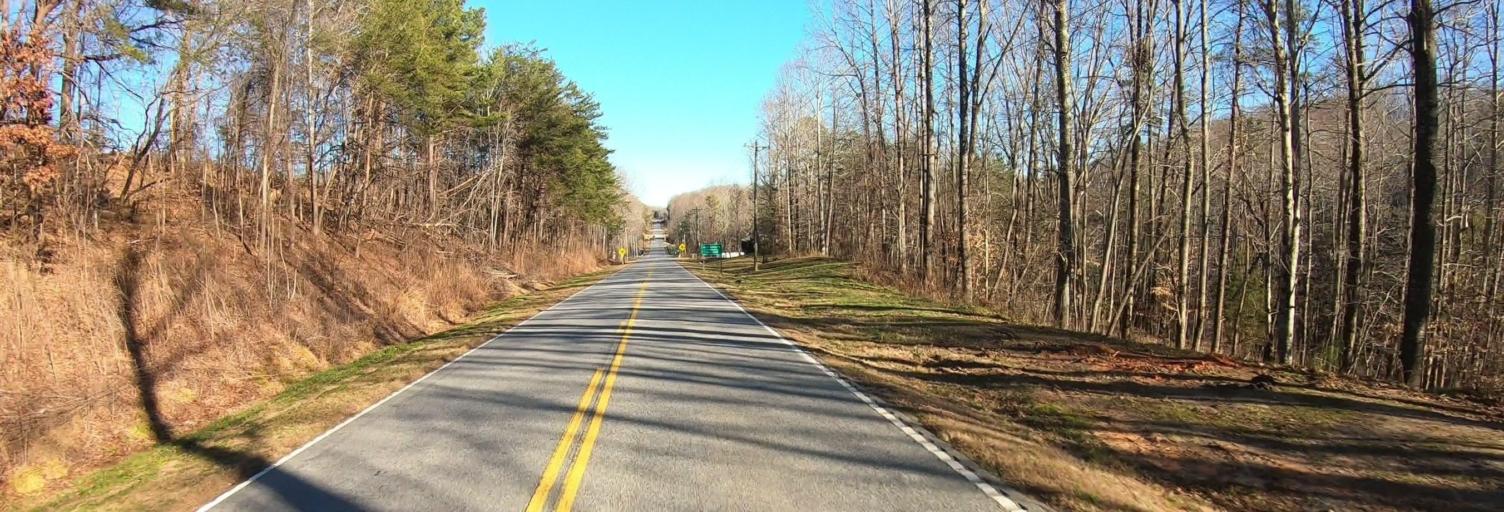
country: US
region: South Carolina
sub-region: Greenville County
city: Tigerville
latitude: 35.1040
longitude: -82.3749
